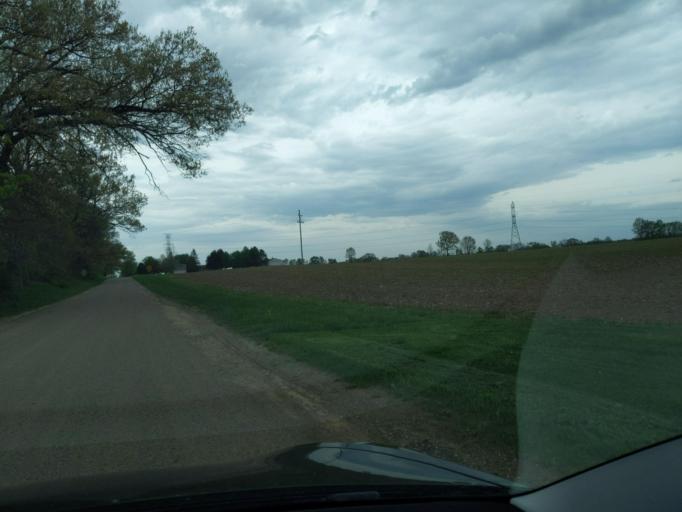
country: US
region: Michigan
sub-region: Ingham County
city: Stockbridge
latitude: 42.4137
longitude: -84.1361
